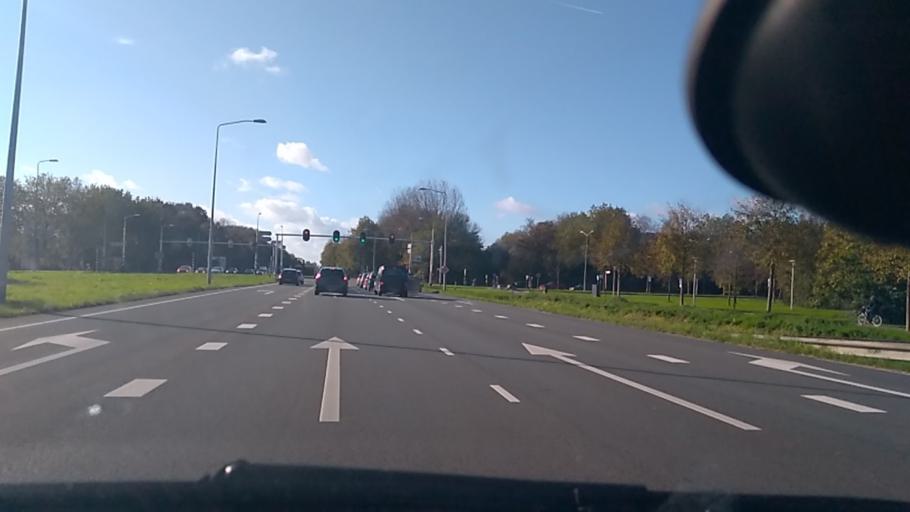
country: NL
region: North Holland
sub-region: Gemeente Hoorn
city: Hoorn
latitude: 52.6539
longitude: 5.0671
